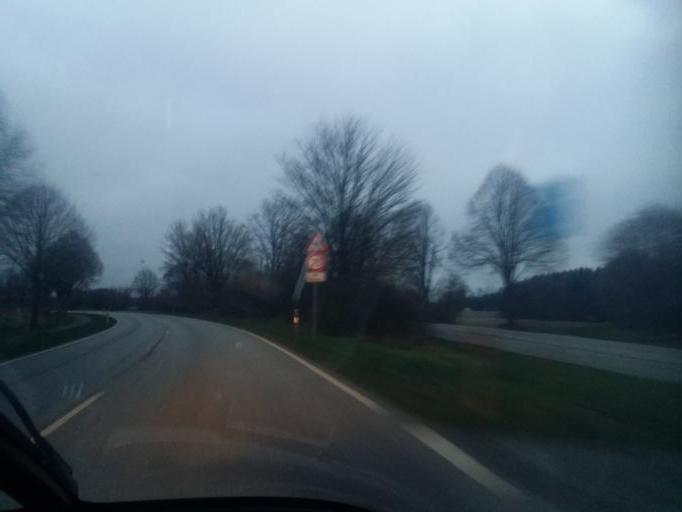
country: DE
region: Schleswig-Holstein
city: Gokels
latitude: 54.1176
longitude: 9.4493
